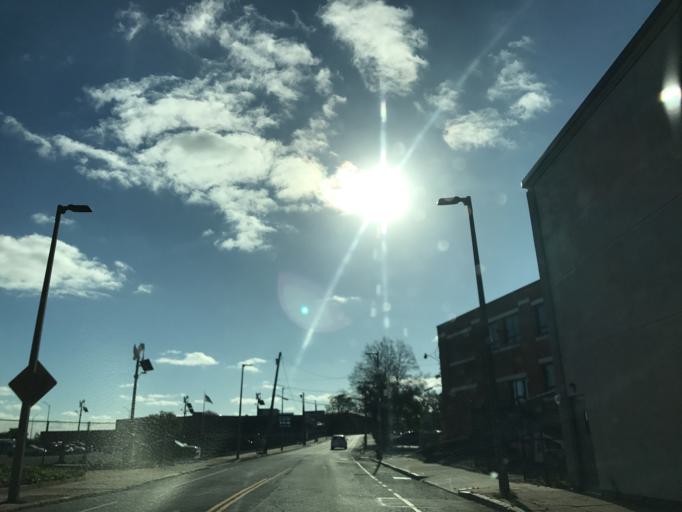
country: US
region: Massachusetts
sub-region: Suffolk County
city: South Boston
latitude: 42.3042
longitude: -71.0552
